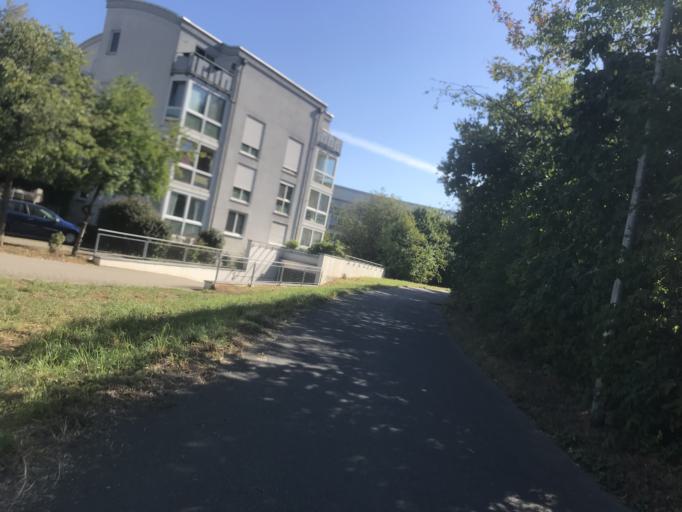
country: DE
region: Hesse
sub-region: Regierungsbezirk Darmstadt
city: Hochheim am Main
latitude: 49.9964
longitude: 8.3368
